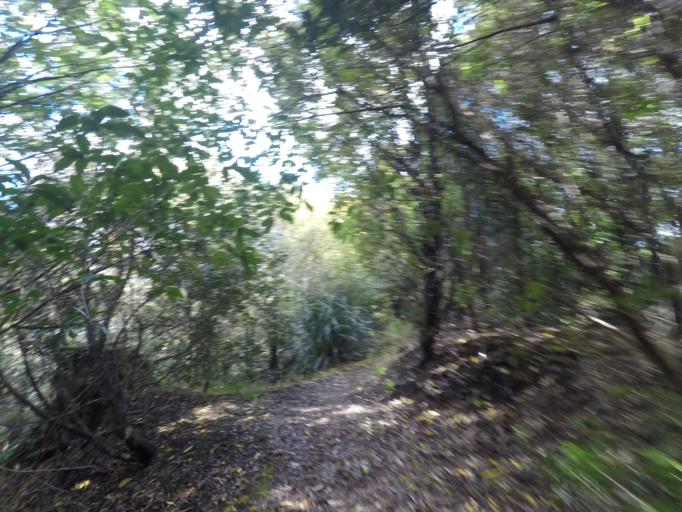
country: NZ
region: Auckland
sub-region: Auckland
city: Rosebank
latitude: -36.8793
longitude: 174.6658
